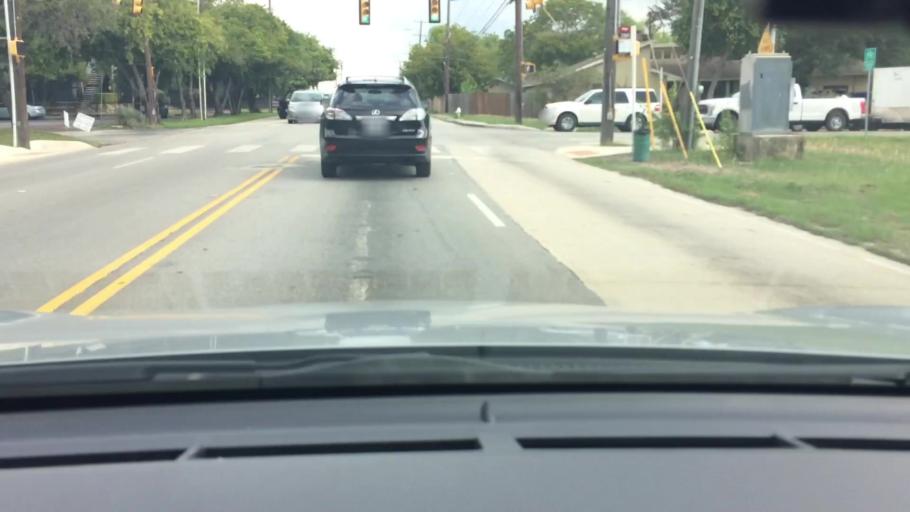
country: US
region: Texas
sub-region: Bexar County
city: Castle Hills
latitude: 29.5446
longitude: -98.5326
